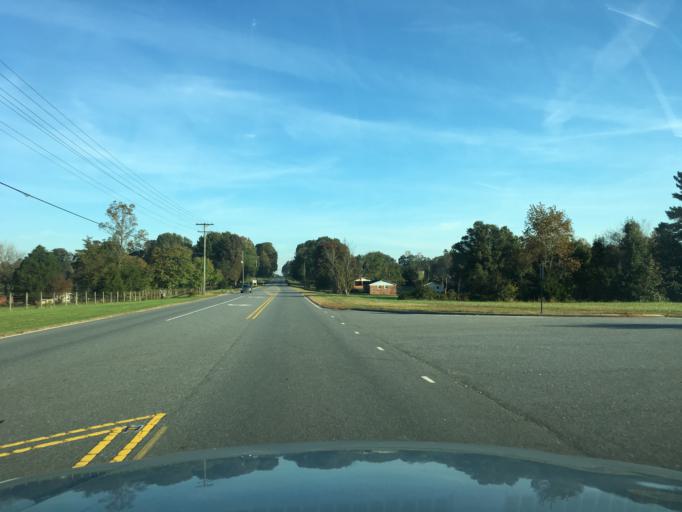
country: US
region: North Carolina
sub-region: Catawba County
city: Maiden
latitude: 35.5995
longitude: -81.2550
